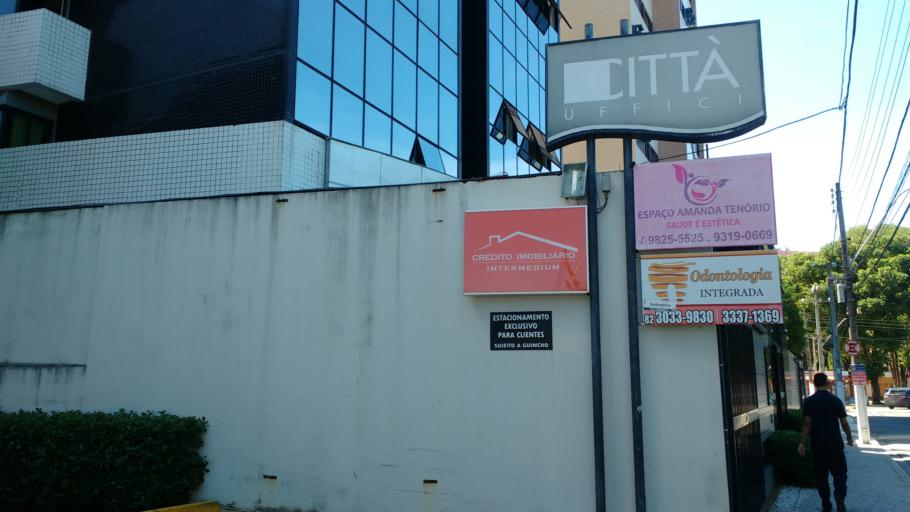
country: BR
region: Alagoas
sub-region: Maceio
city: Maceio
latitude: -9.6634
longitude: -35.7102
